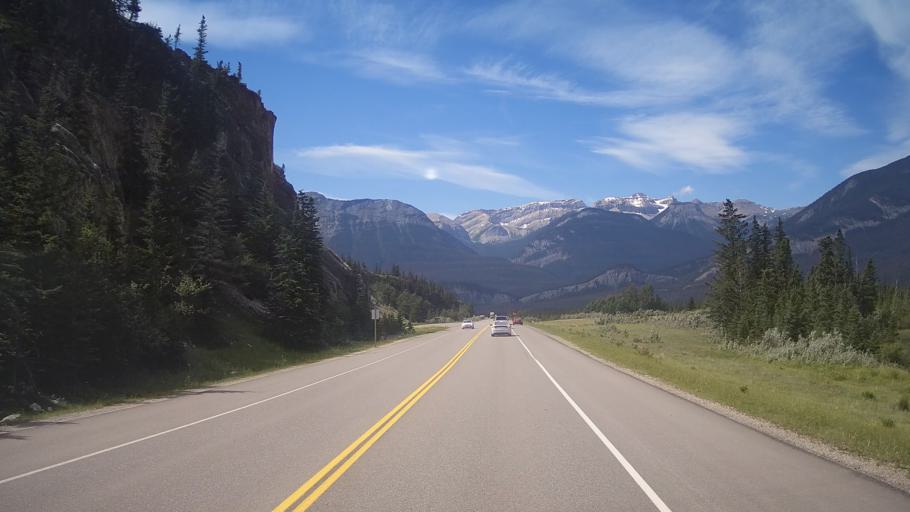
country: CA
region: Alberta
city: Jasper Park Lodge
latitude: 53.0461
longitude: -118.0807
